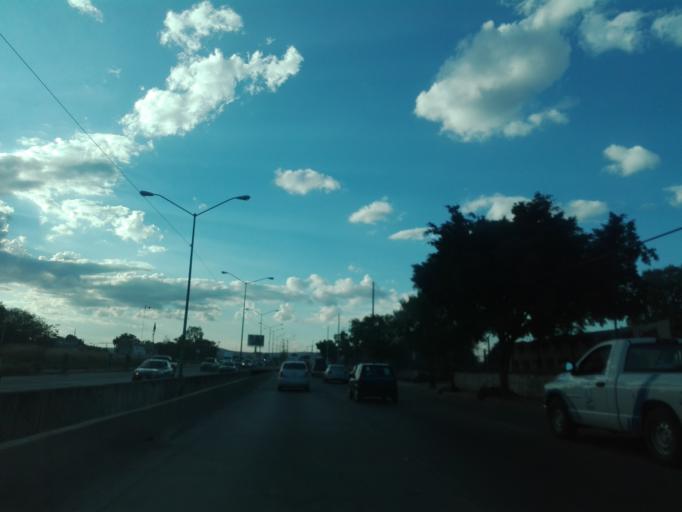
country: MX
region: Guanajuato
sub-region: Leon
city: San Jose de Duran (Los Troncoso)
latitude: 21.0880
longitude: -101.6725
